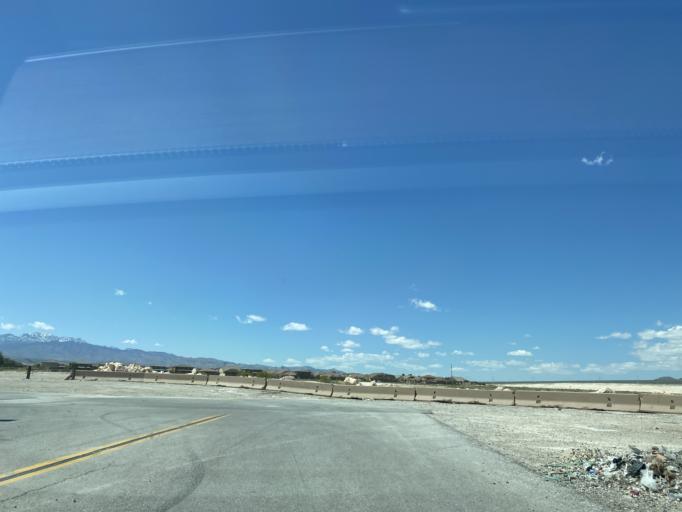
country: US
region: Nevada
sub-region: Clark County
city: North Las Vegas
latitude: 36.3208
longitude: -115.2110
